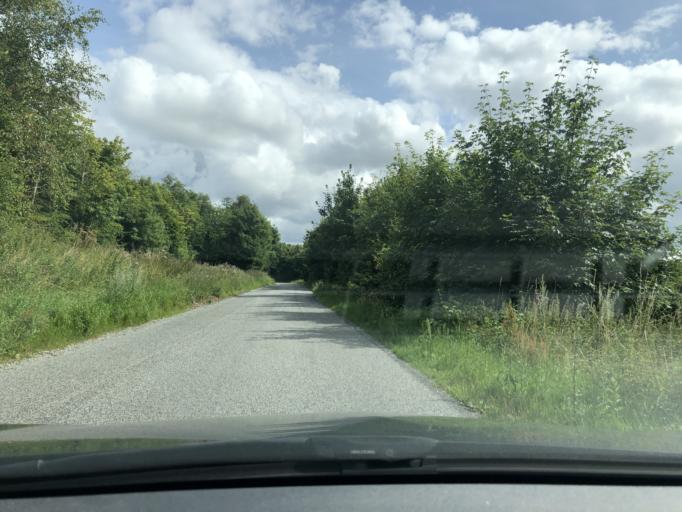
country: DK
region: South Denmark
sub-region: Vejle Kommune
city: Jelling
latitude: 55.6984
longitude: 9.4444
